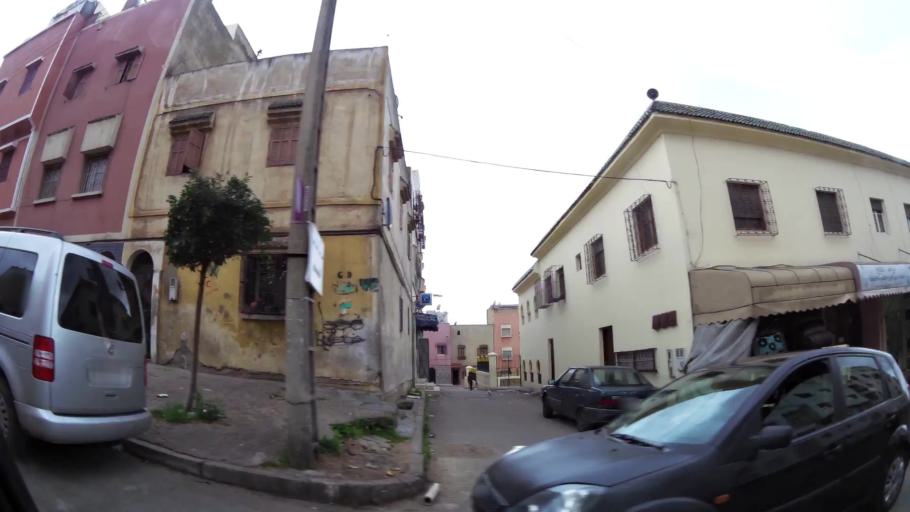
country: MA
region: Grand Casablanca
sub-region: Mediouna
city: Tit Mellil
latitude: 33.5700
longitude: -7.5393
